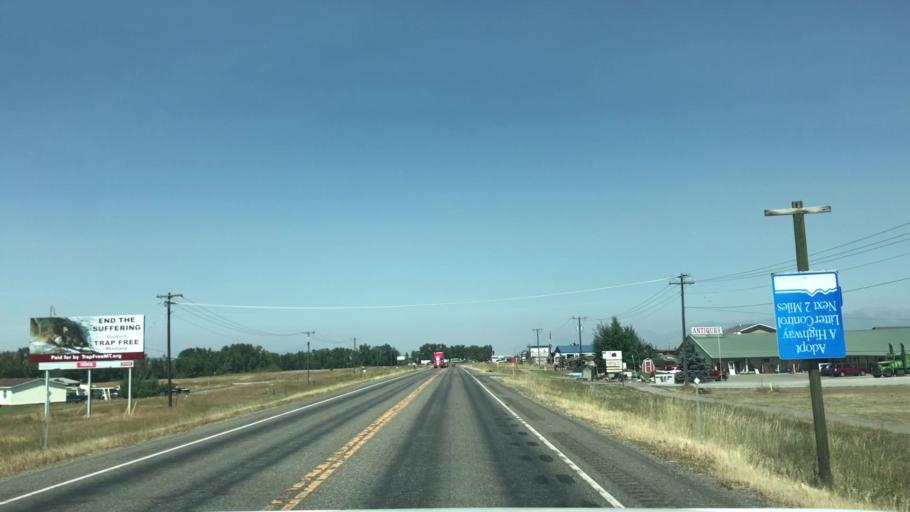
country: US
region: Montana
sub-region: Gallatin County
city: Four Corners
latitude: 45.6019
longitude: -111.1962
